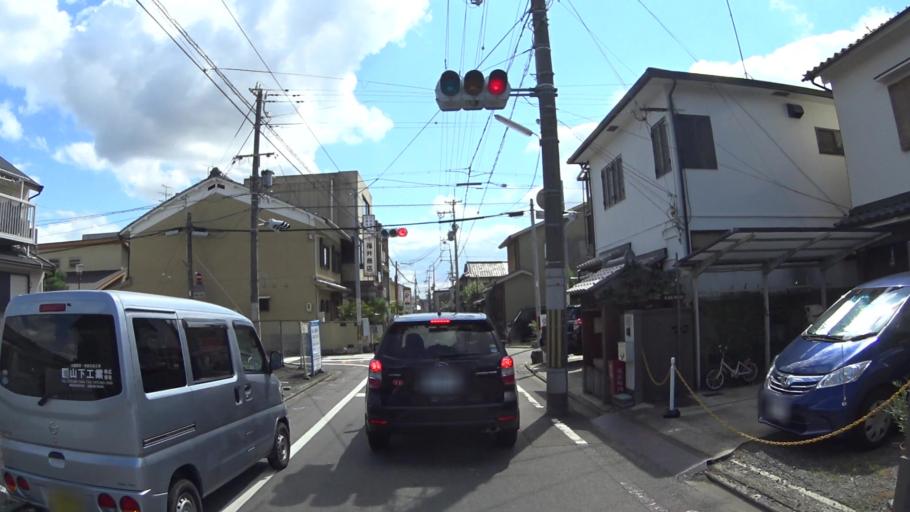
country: JP
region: Kyoto
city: Muko
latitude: 34.9427
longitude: 135.7580
